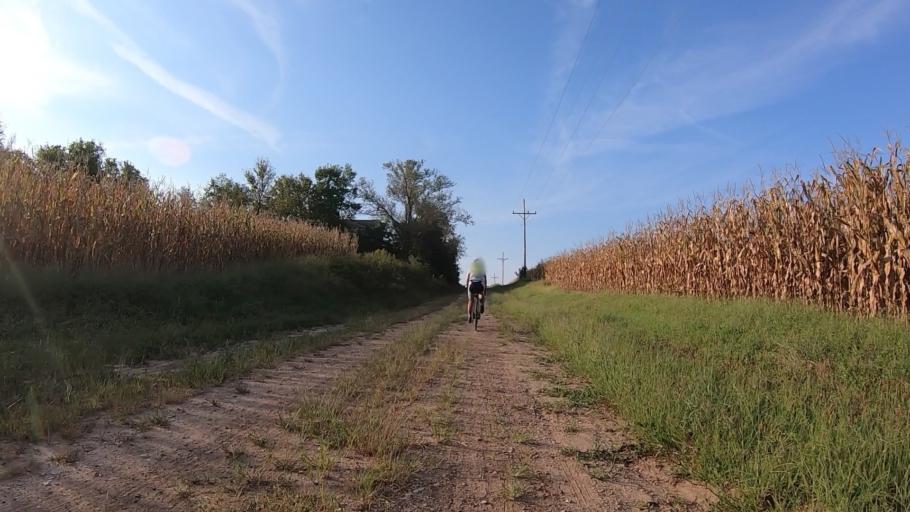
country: US
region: Kansas
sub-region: Marshall County
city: Blue Rapids
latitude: 39.7101
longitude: -96.7793
